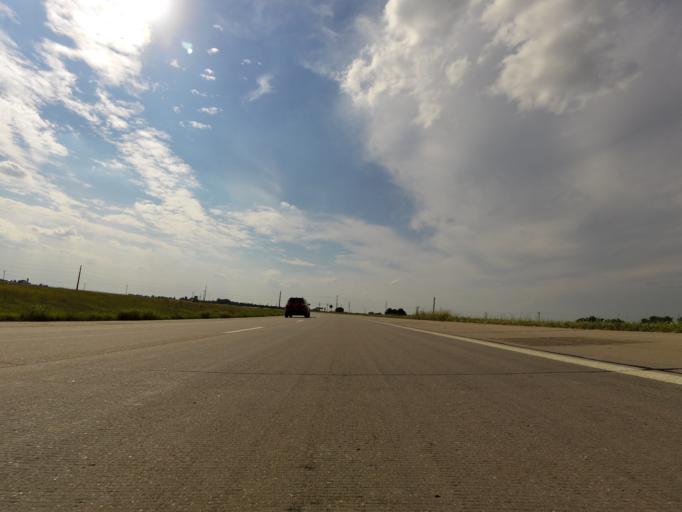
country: US
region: Kansas
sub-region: Sedgwick County
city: Colwich
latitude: 37.8234
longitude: -97.5141
